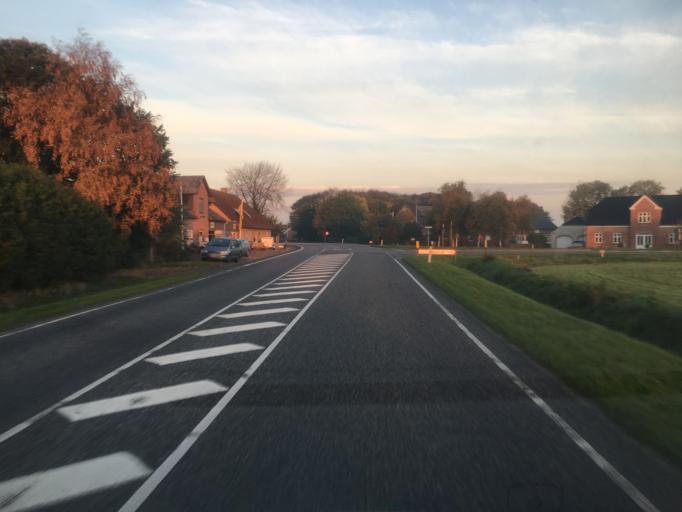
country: DK
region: South Denmark
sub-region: Tonder Kommune
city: Logumkloster
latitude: 55.0392
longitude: 9.0272
